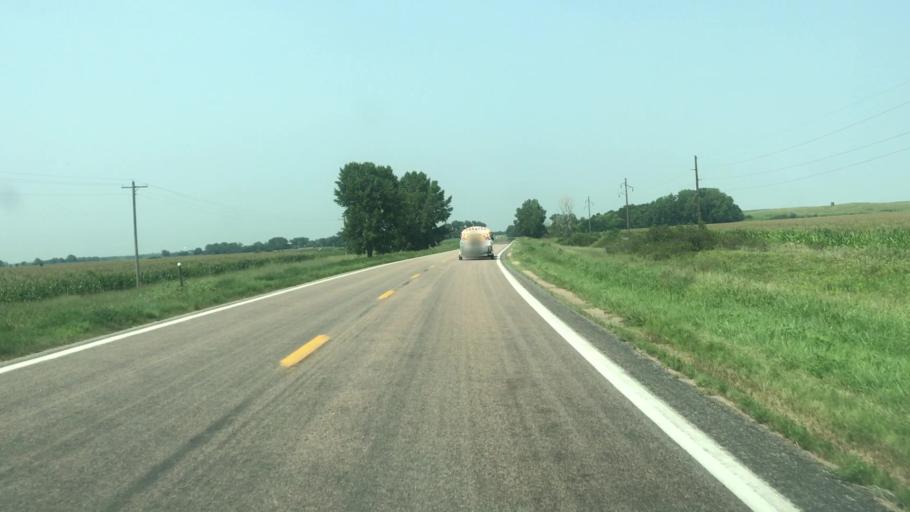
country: US
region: Nebraska
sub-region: Sherman County
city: Loup City
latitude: 41.2369
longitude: -98.9385
